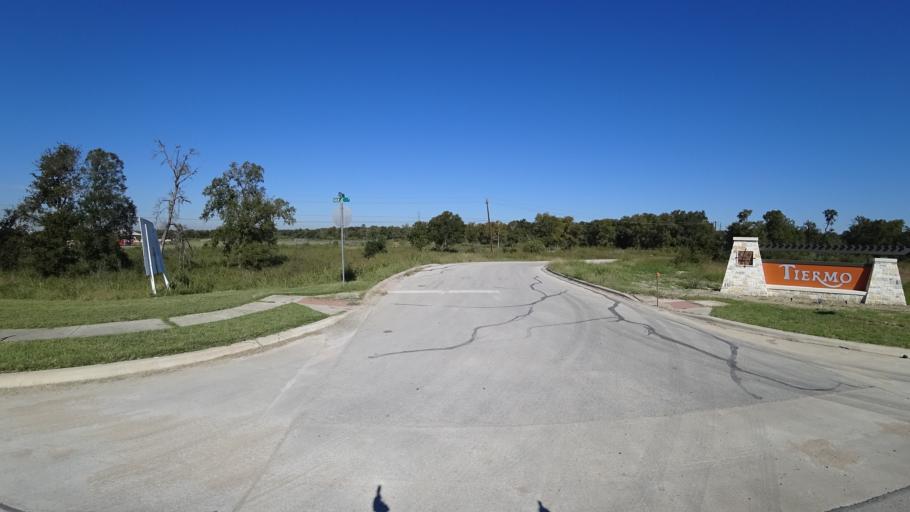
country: US
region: Texas
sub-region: Travis County
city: Hornsby Bend
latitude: 30.2590
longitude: -97.5903
